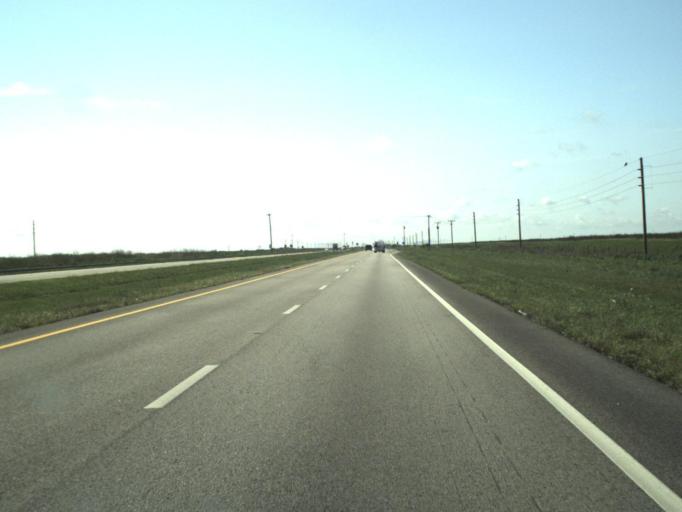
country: US
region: Florida
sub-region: Palm Beach County
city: Belle Glade Camp
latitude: 26.3797
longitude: -80.5727
